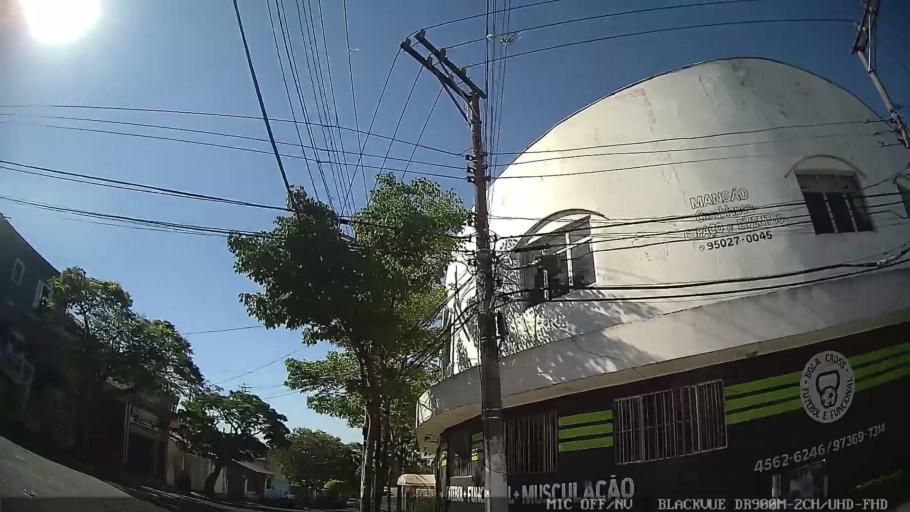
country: BR
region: Sao Paulo
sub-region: Guarulhos
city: Guarulhos
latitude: -23.5322
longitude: -46.5105
